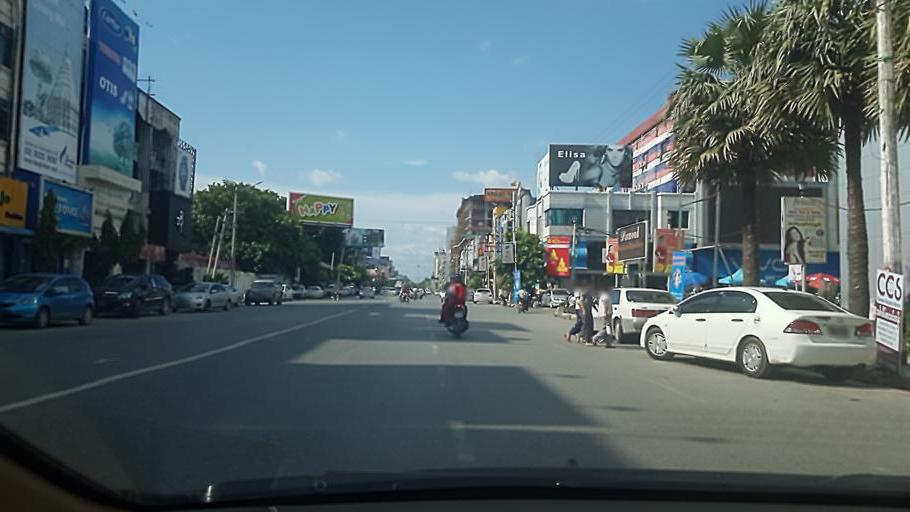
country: MM
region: Mandalay
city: Mandalay
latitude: 21.9718
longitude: 96.0866
